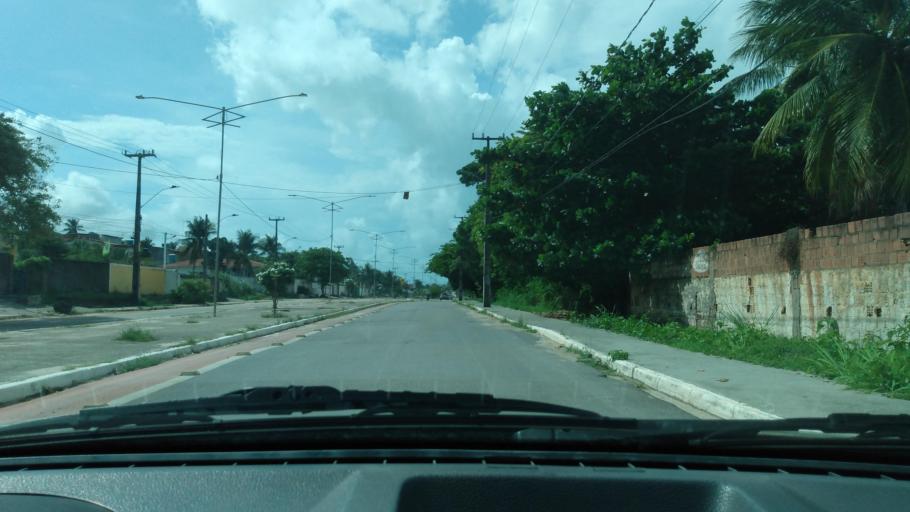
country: BR
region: Pernambuco
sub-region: Cabo De Santo Agostinho
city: Cabo
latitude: -8.3179
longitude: -34.9509
